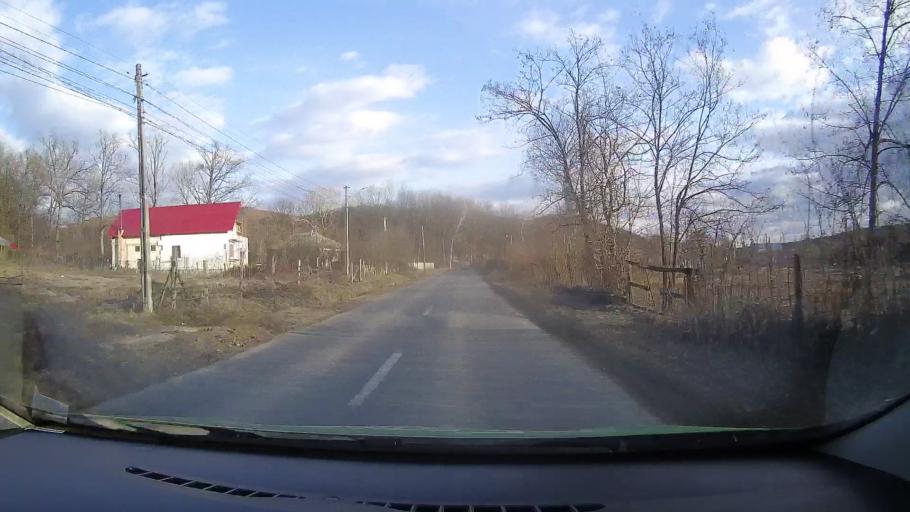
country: RO
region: Dambovita
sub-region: Comuna Ocnita
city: Ocnita
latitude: 44.9643
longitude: 25.5480
